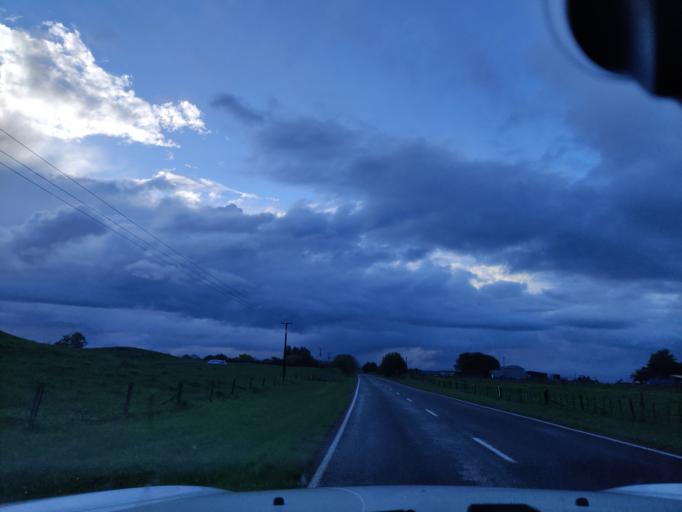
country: NZ
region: Waikato
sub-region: South Waikato District
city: Tokoroa
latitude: -38.2337
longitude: 175.8378
